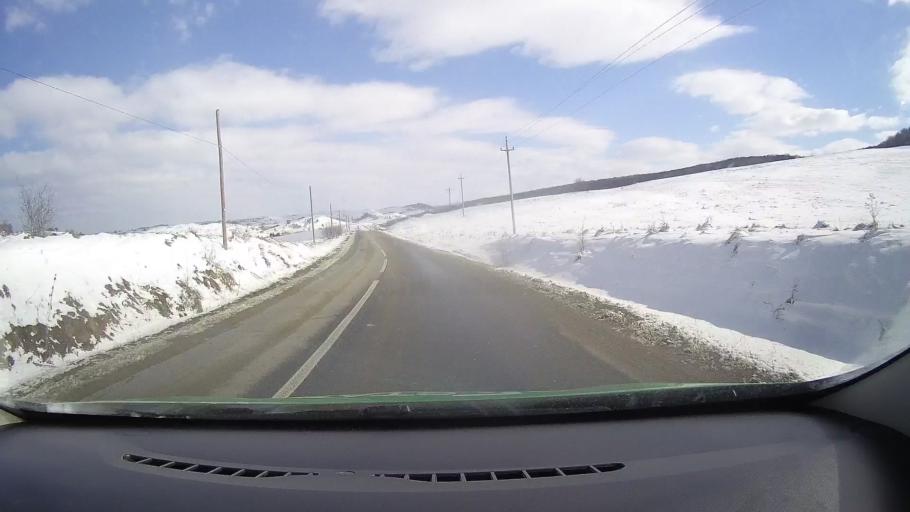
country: RO
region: Sibiu
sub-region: Comuna Barghis
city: Barghis
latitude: 45.9799
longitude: 24.5134
